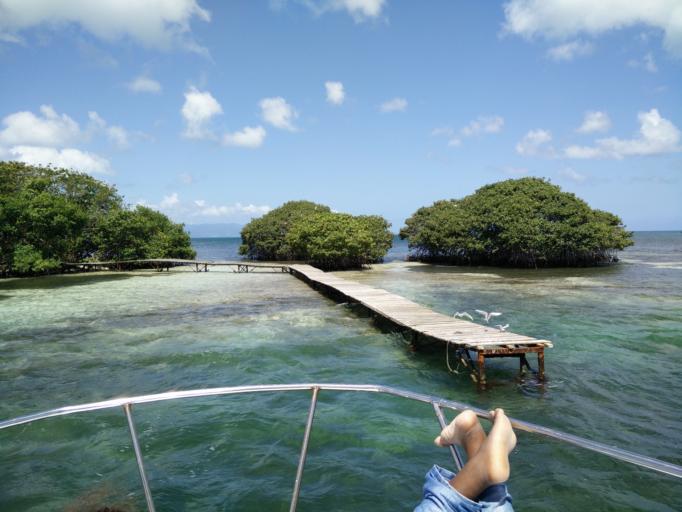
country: GP
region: Guadeloupe
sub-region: Guadeloupe
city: Petit-Canal
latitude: 16.3667
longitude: -61.5067
